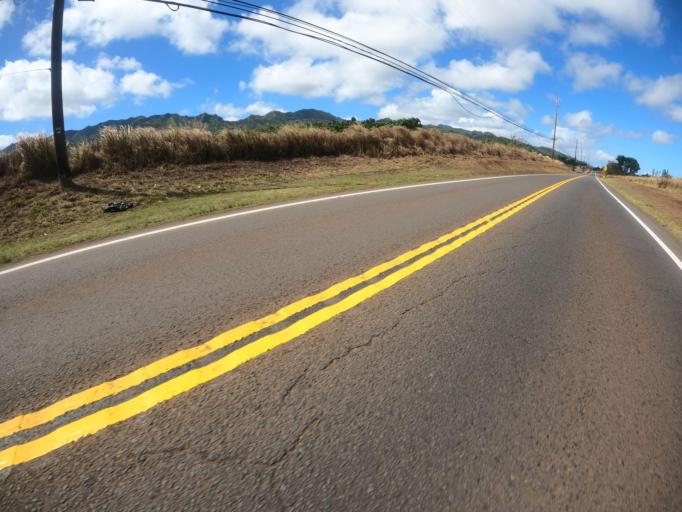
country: US
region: Hawaii
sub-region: Honolulu County
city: Village Park
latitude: 21.4279
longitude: -158.0553
